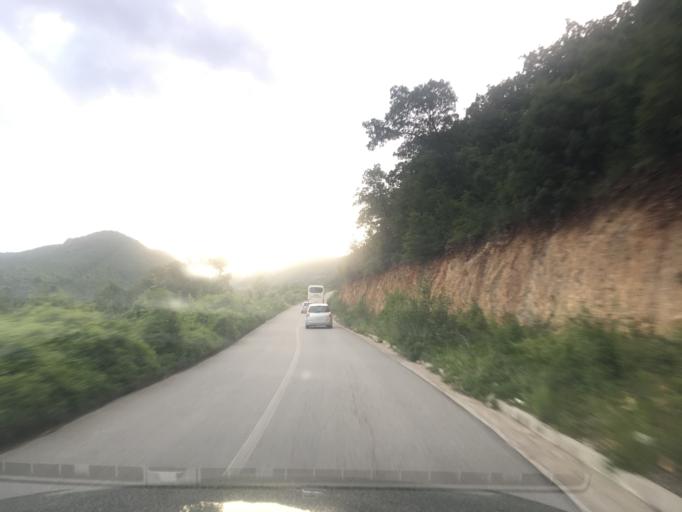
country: XK
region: Ferizaj
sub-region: Hani i Elezit
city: Hani i Elezit
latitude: 42.1451
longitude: 21.2846
